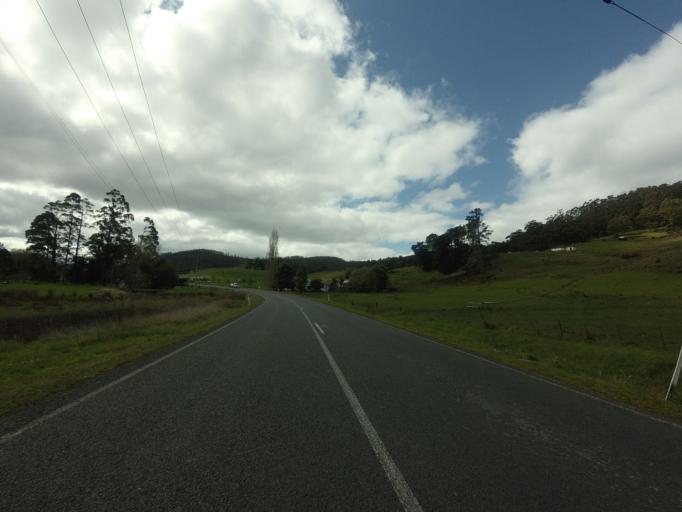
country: AU
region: Tasmania
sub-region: Huon Valley
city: Cygnet
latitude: -43.2964
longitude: 147.0111
